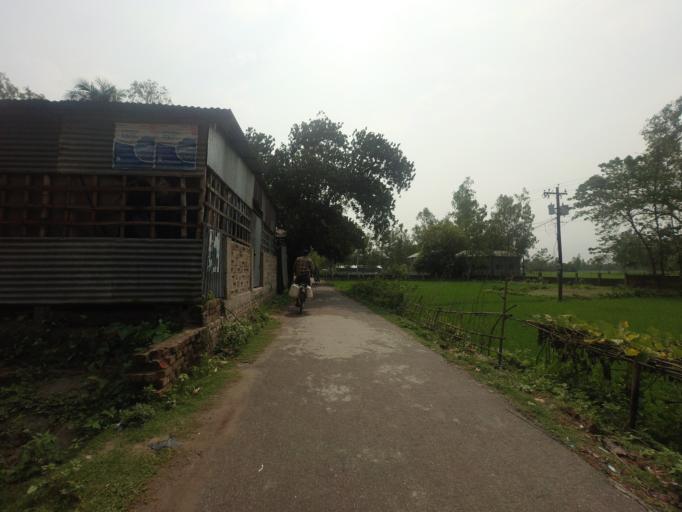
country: BD
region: Rajshahi
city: Sirajganj
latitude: 24.3238
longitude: 89.6840
